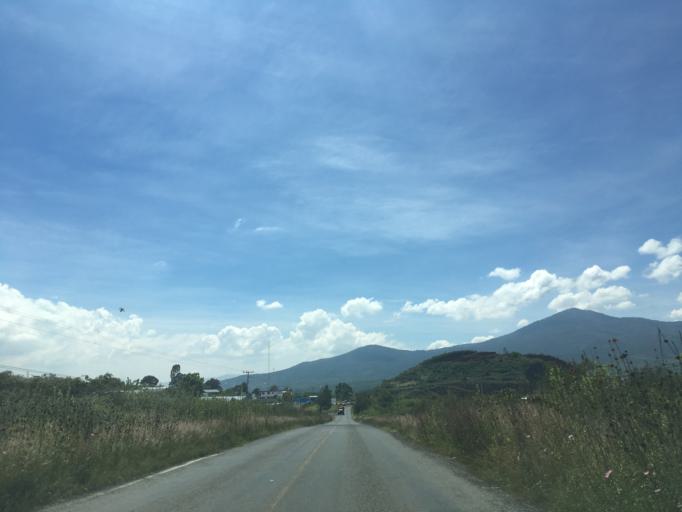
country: MX
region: Michoacan
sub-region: Morelia
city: Lomas de la Maestranza
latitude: 19.7021
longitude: -101.3400
